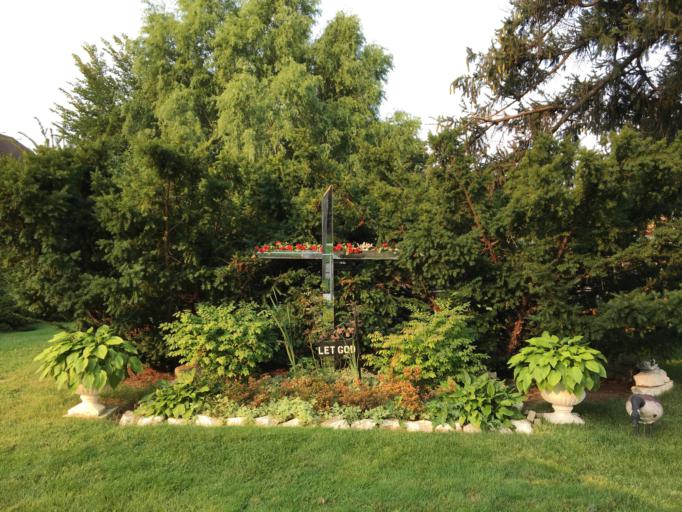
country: US
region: Michigan
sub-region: Wayne County
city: Grosse Pointe Park
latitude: 42.3881
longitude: -82.9887
